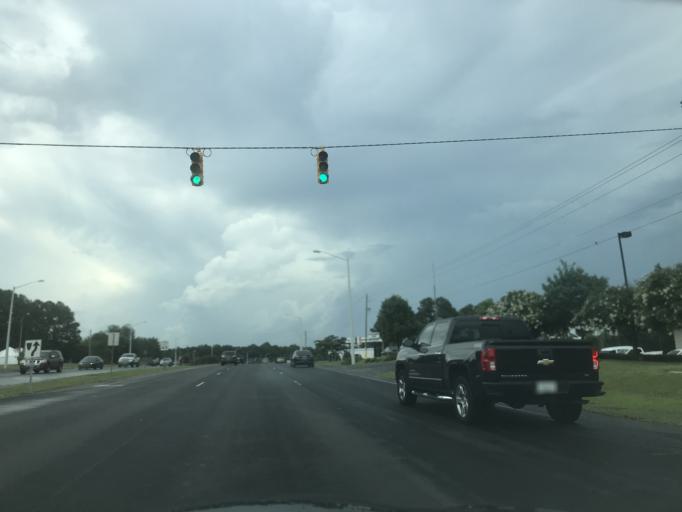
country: US
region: North Carolina
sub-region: Johnston County
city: Clayton
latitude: 35.6436
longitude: -78.4558
